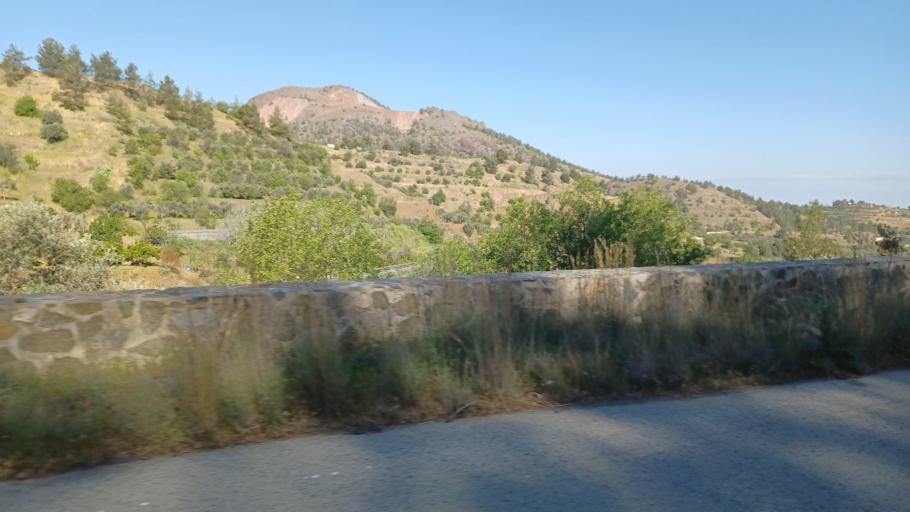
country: CY
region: Limassol
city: Kyperounta
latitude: 35.0257
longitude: 33.0373
